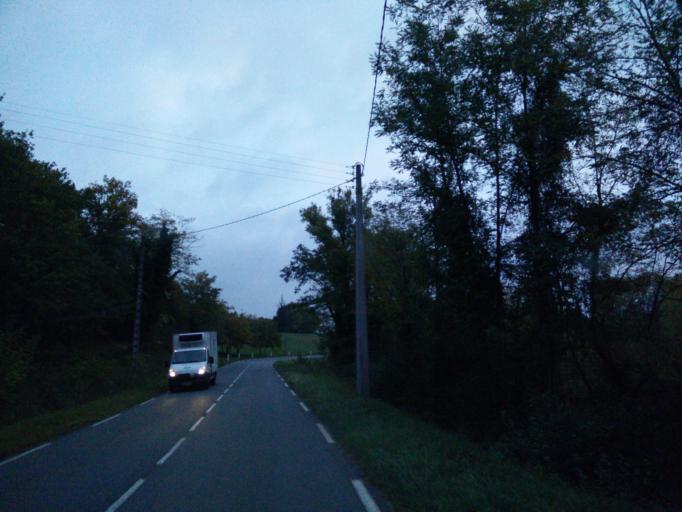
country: FR
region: Aquitaine
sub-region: Departement de la Dordogne
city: Sarlat-la-Caneda
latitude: 44.9071
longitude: 1.1839
